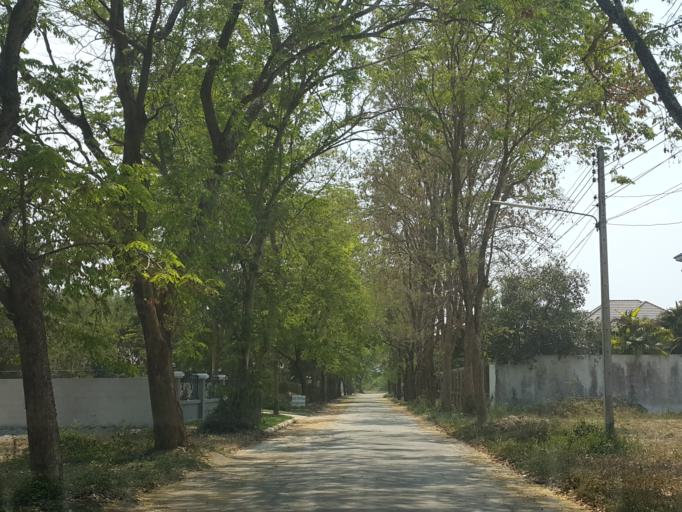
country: TH
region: Chiang Mai
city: Saraphi
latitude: 18.7289
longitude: 98.9761
